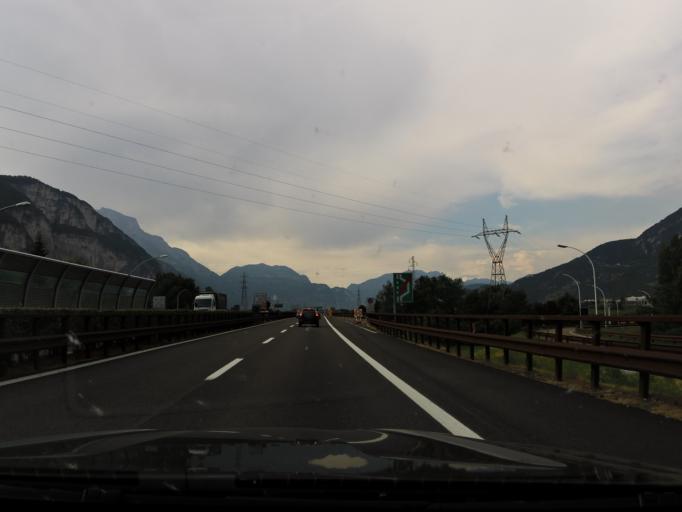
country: IT
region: Trentino-Alto Adige
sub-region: Provincia di Trento
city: Trento
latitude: 46.0760
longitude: 11.1065
